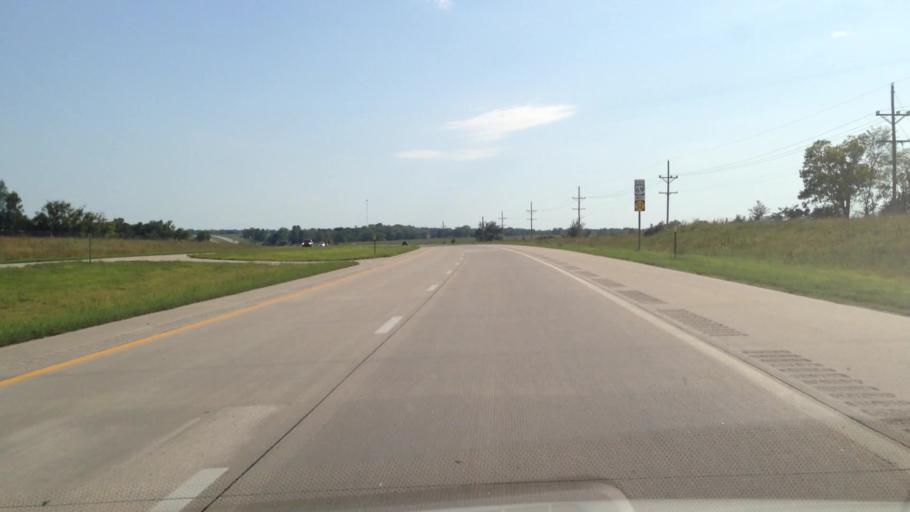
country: US
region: Kansas
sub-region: Linn County
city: Pleasanton
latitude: 38.2126
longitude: -94.7044
